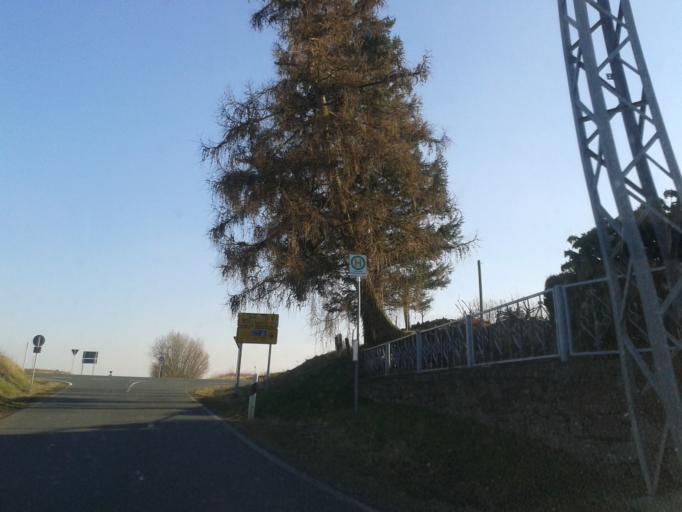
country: DE
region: Saxony
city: Nossen
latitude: 51.0244
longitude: 13.3135
